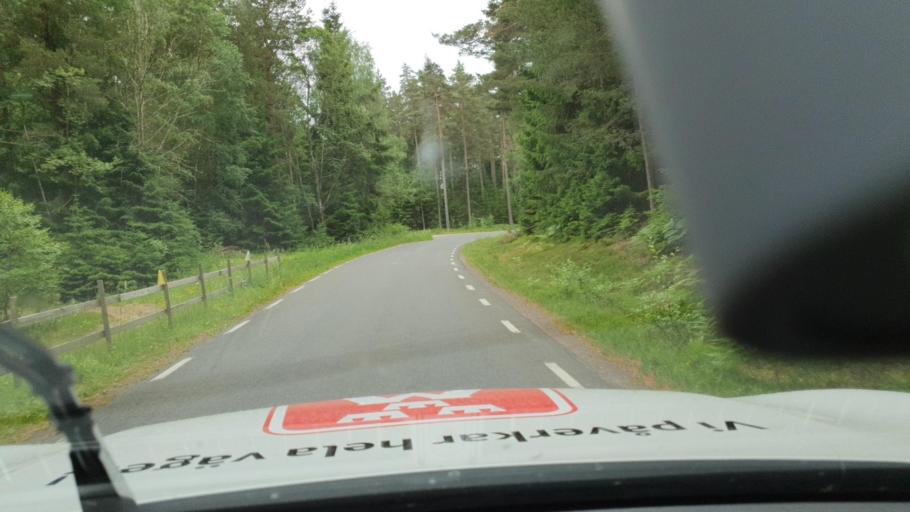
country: SE
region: Vaestra Goetaland
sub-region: Tibro Kommun
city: Tibro
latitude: 58.3341
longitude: 14.1954
